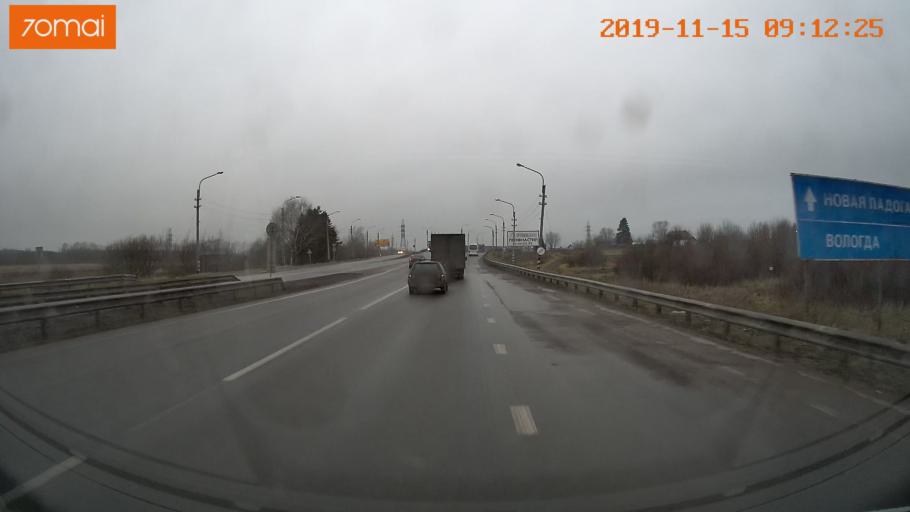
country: RU
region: Vologda
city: Tonshalovo
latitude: 59.2079
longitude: 37.9372
